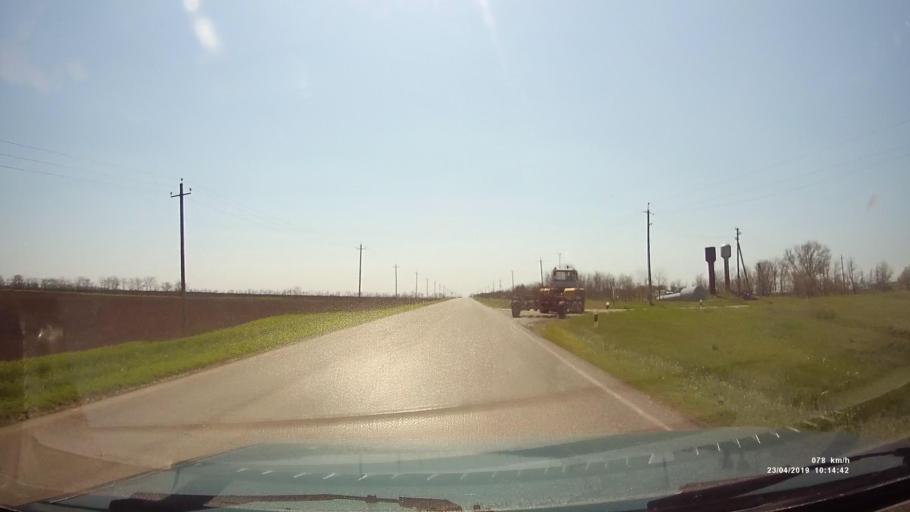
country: RU
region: Rostov
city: Sovetskoye
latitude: 46.6743
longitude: 42.3729
